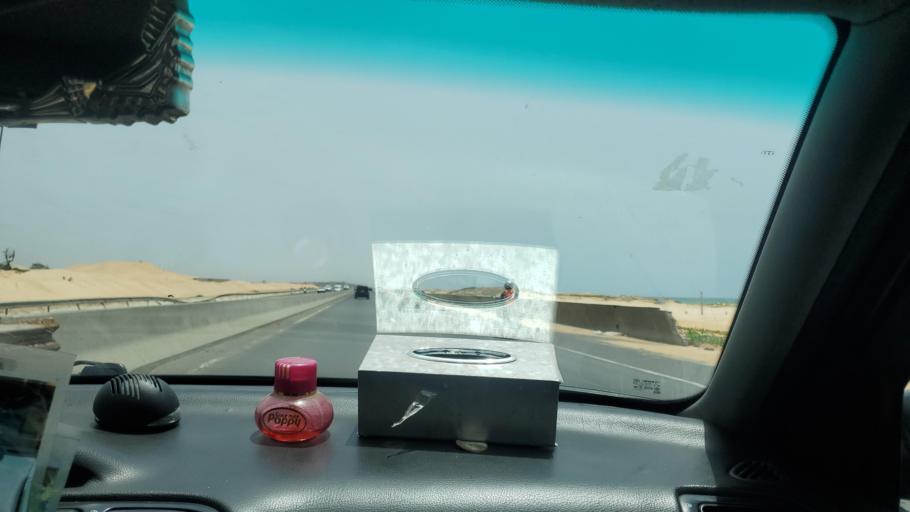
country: SN
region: Dakar
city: Pikine
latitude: 14.8009
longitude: -17.3522
